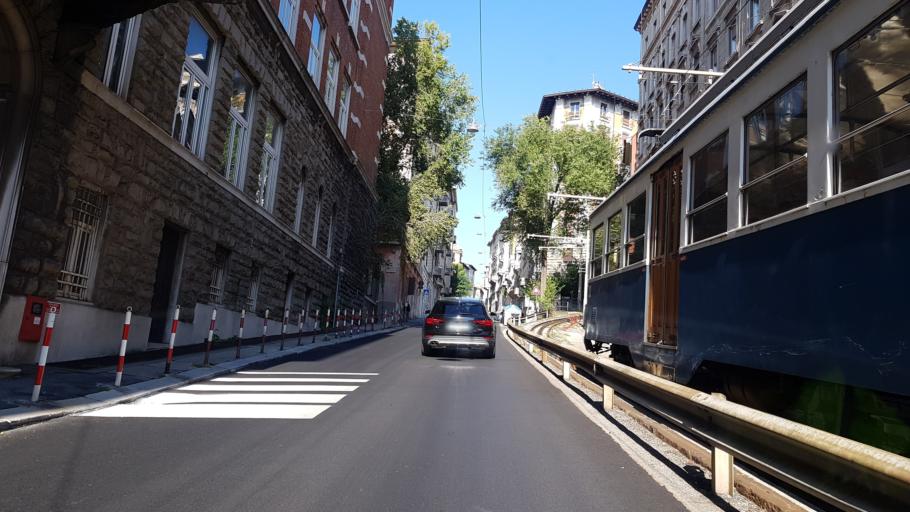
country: IT
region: Friuli Venezia Giulia
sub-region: Provincia di Trieste
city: Trieste
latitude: 45.6572
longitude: 13.7769
